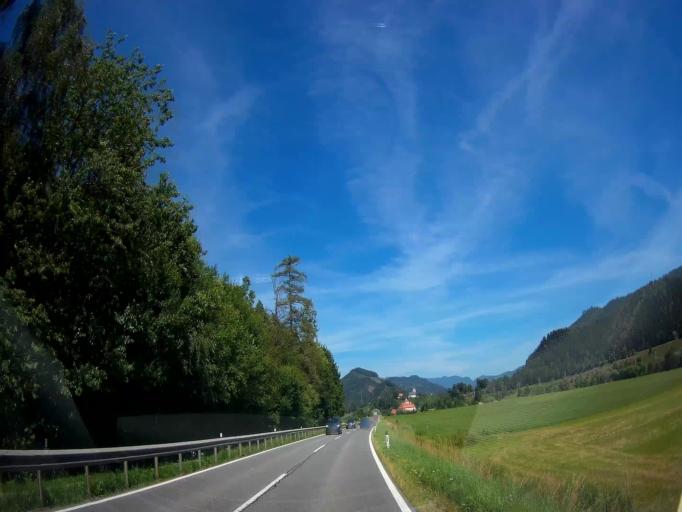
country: AT
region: Carinthia
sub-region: Politischer Bezirk Sankt Veit an der Glan
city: Althofen
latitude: 46.8828
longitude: 14.4456
